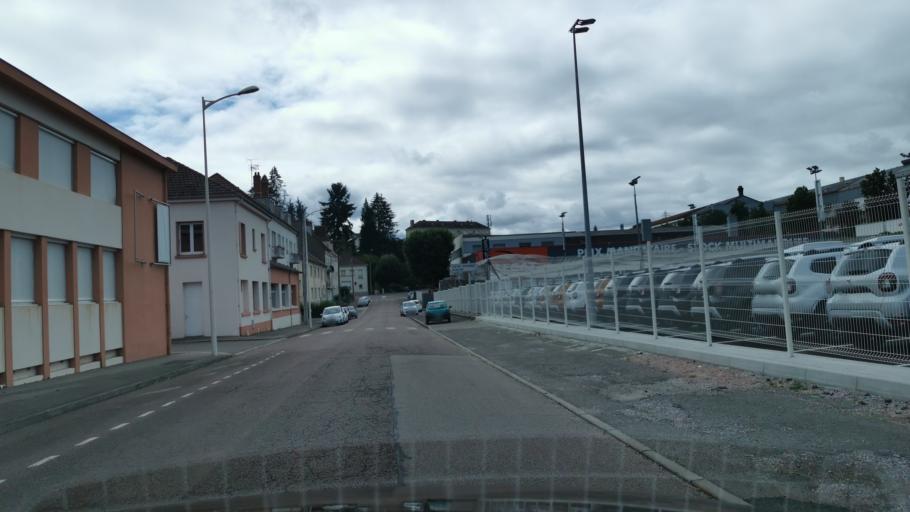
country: FR
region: Bourgogne
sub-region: Departement de Saone-et-Loire
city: Le Creusot
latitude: 46.8034
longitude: 4.4370
